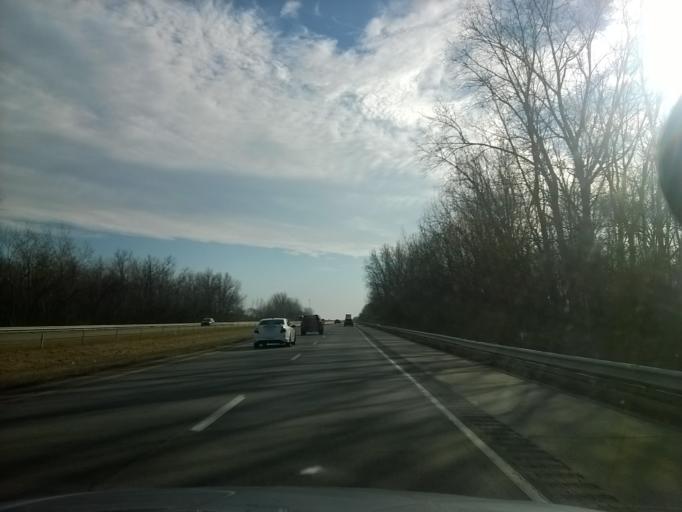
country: US
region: Indiana
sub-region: Johnson County
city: Edinburgh
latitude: 39.3942
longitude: -85.9432
